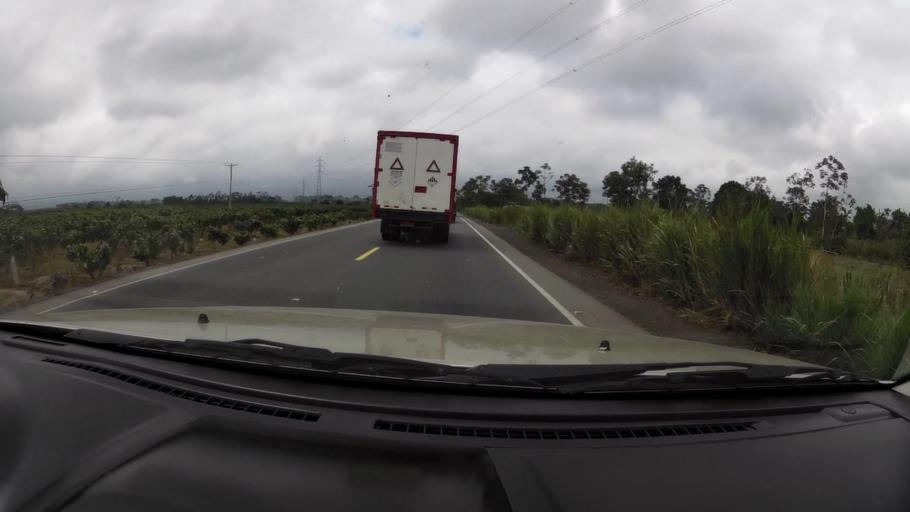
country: EC
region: Guayas
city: Balao
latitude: -2.8948
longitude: -79.7057
